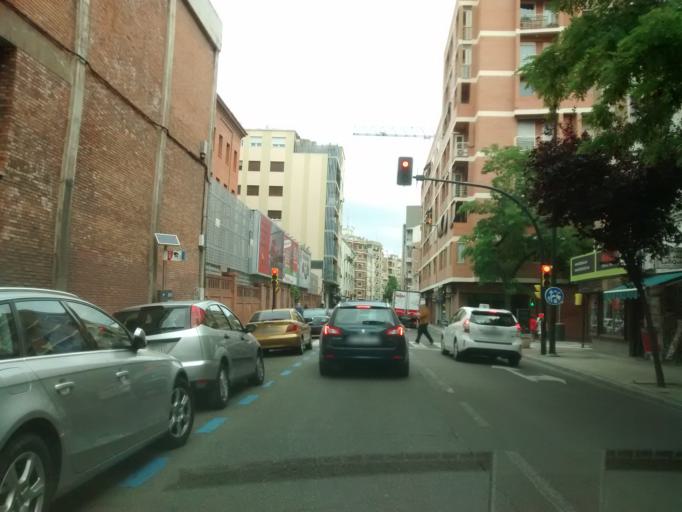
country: ES
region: Aragon
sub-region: Provincia de Zaragoza
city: Delicias
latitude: 41.6458
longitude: -0.8921
